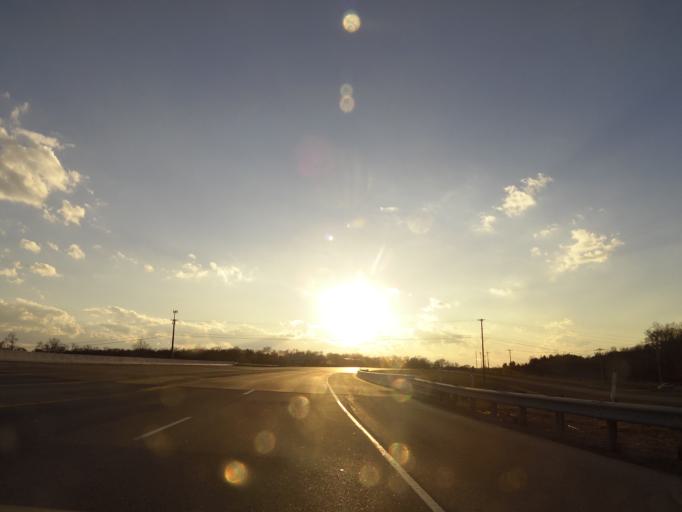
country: US
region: Tennessee
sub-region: Wilson County
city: Mount Juliet
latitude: 36.2332
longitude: -86.4281
